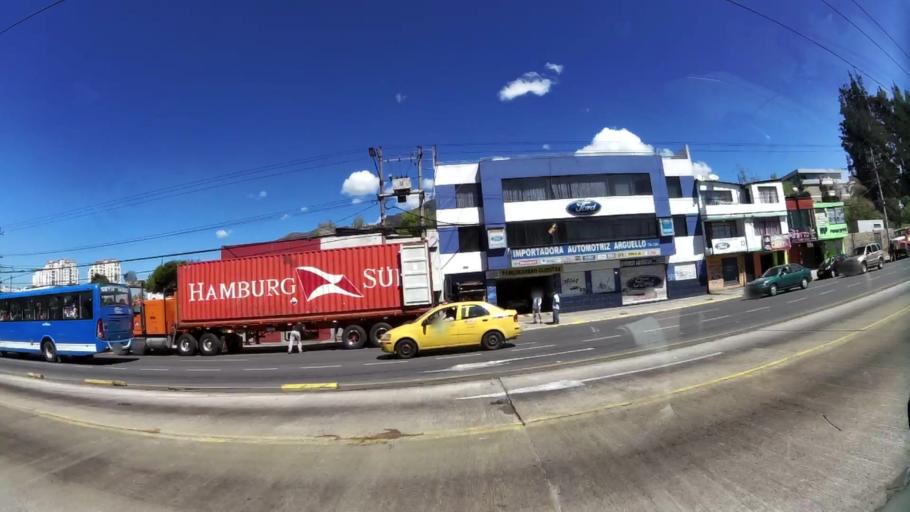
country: EC
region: Pichincha
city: Quito
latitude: -0.1610
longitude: -78.4875
